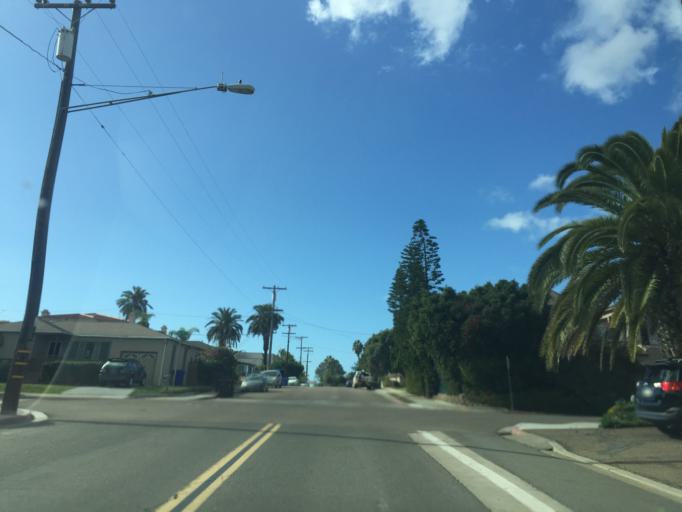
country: US
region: California
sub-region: San Diego County
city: La Jolla
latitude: 32.7959
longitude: -117.2315
